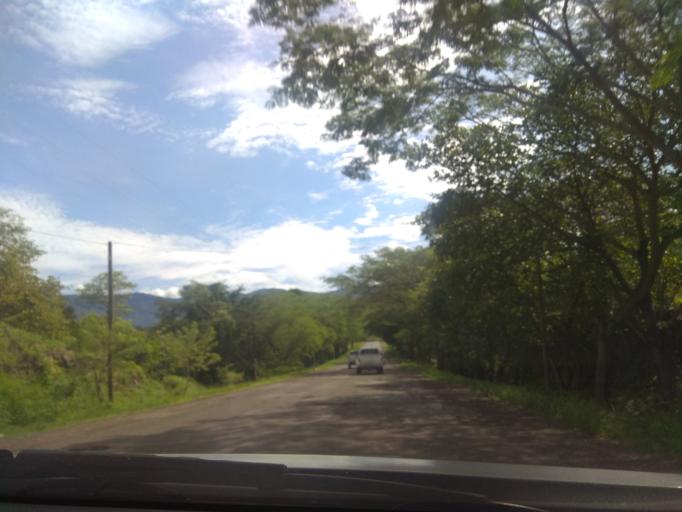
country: HN
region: Intibuca
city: Jesus de Otoro
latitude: 14.4626
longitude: -88.0096
